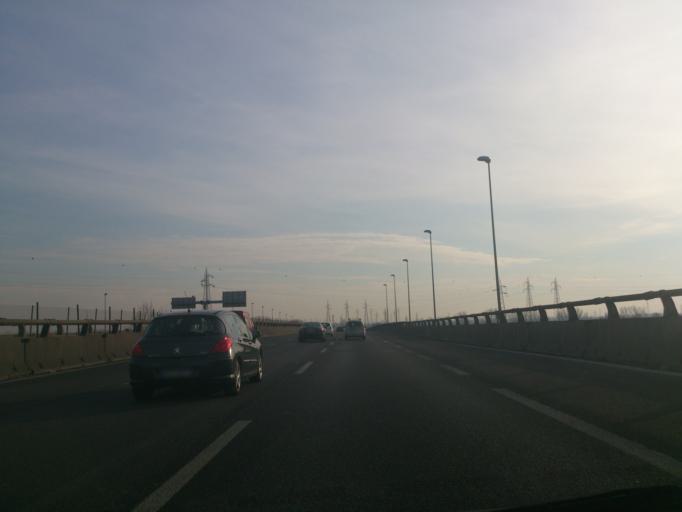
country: IT
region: Lombardy
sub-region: Citta metropolitana di Milano
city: Chiaravalle
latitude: 45.4245
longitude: 9.2455
